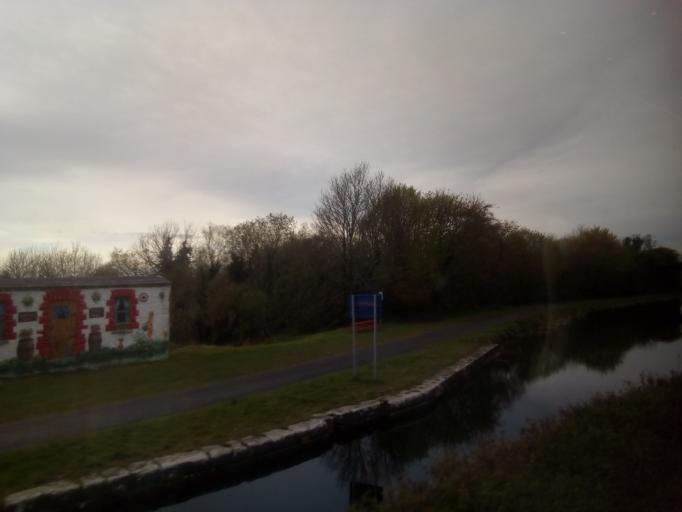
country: IE
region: Leinster
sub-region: Kildare
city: Leixlip
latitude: 53.3737
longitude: -6.5035
